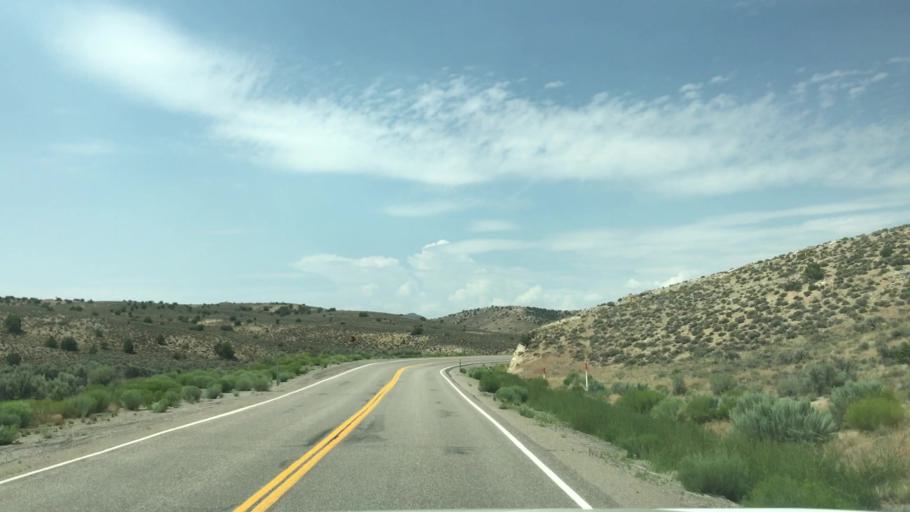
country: US
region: Nevada
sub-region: White Pine County
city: Ely
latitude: 39.3519
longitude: -115.3629
